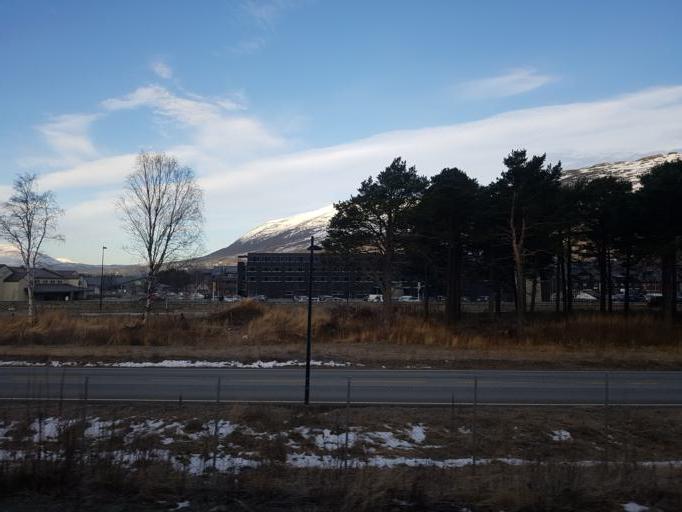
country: NO
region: Sor-Trondelag
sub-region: Oppdal
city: Oppdal
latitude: 62.5914
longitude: 9.6875
